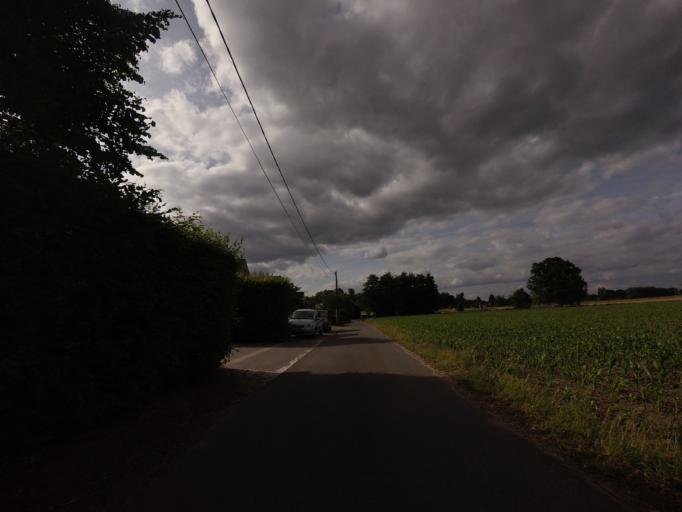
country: BE
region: Flanders
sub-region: Provincie Antwerpen
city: Duffel
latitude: 51.0895
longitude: 4.4706
